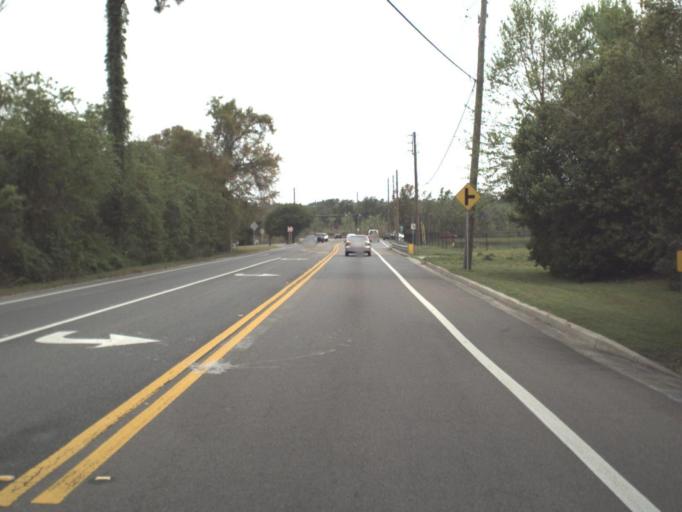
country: US
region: Florida
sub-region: Escambia County
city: East Pensacola Heights
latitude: 30.4820
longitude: -87.1622
